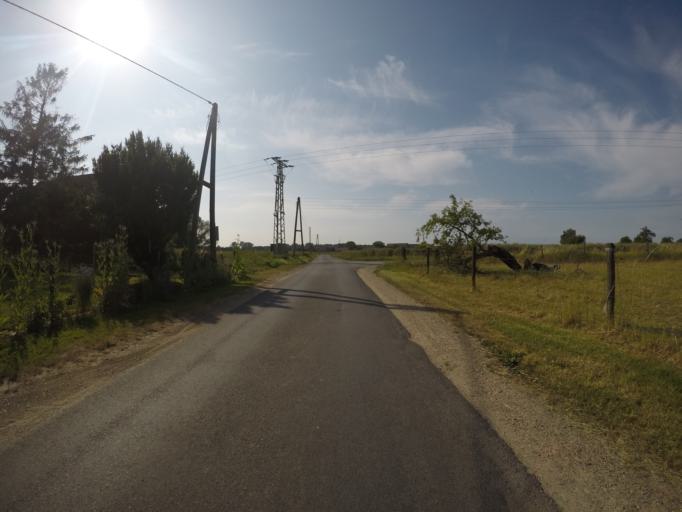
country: DE
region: North Rhine-Westphalia
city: Kalkar
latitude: 51.7354
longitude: 6.3111
